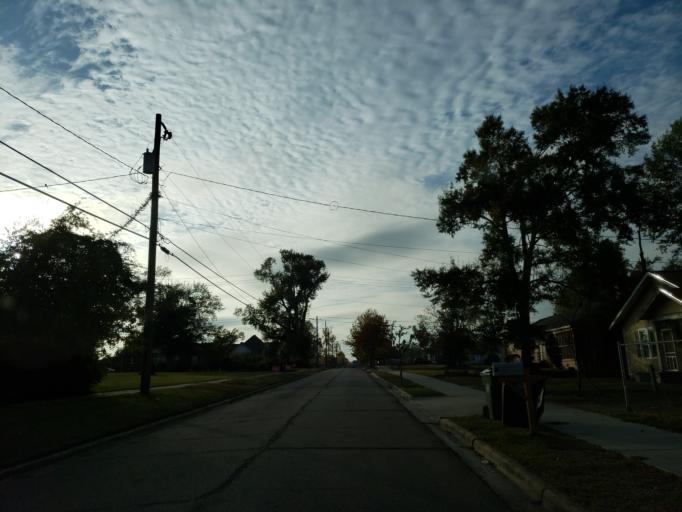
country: US
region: Mississippi
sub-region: Forrest County
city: Hattiesburg
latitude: 31.3062
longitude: -89.2872
